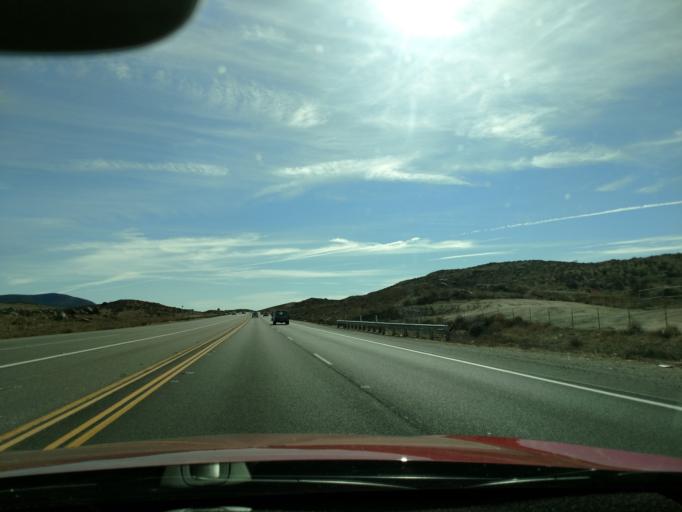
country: US
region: California
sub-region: Riverside County
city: Winchester
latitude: 33.6565
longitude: -117.0846
